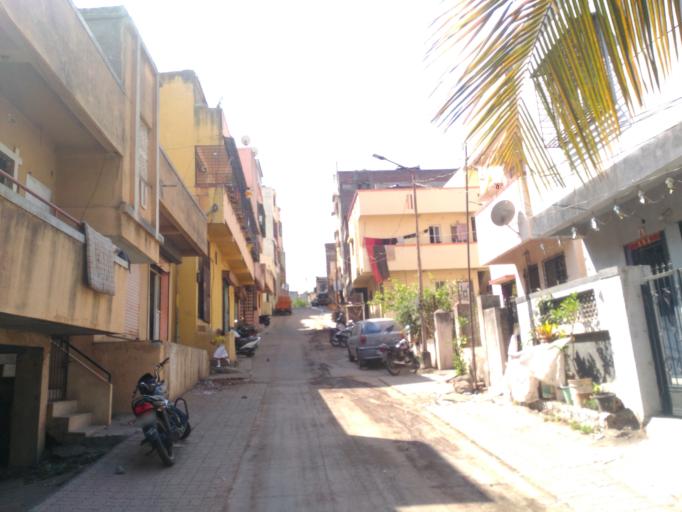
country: IN
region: Maharashtra
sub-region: Pune Division
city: Pune
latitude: 18.4472
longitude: 73.8769
